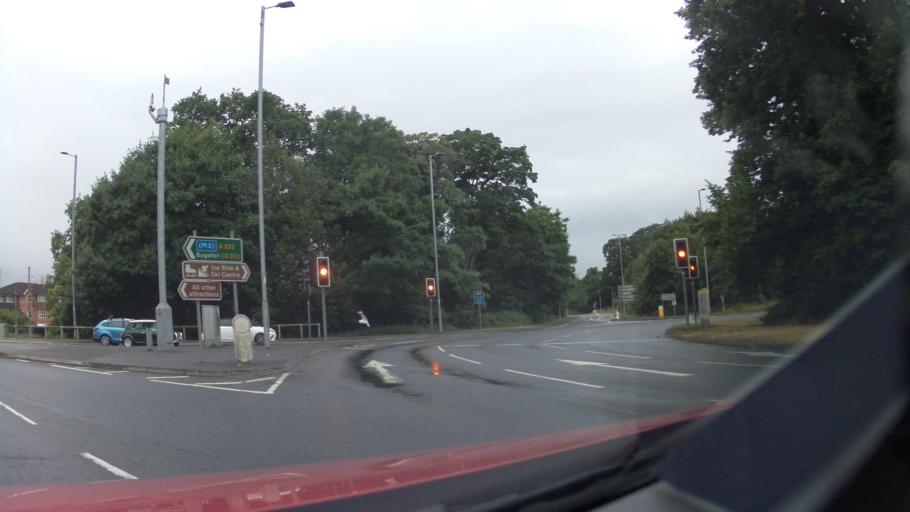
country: GB
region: England
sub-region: Bracknell Forest
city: Bracknell
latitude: 51.4090
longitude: -0.7477
